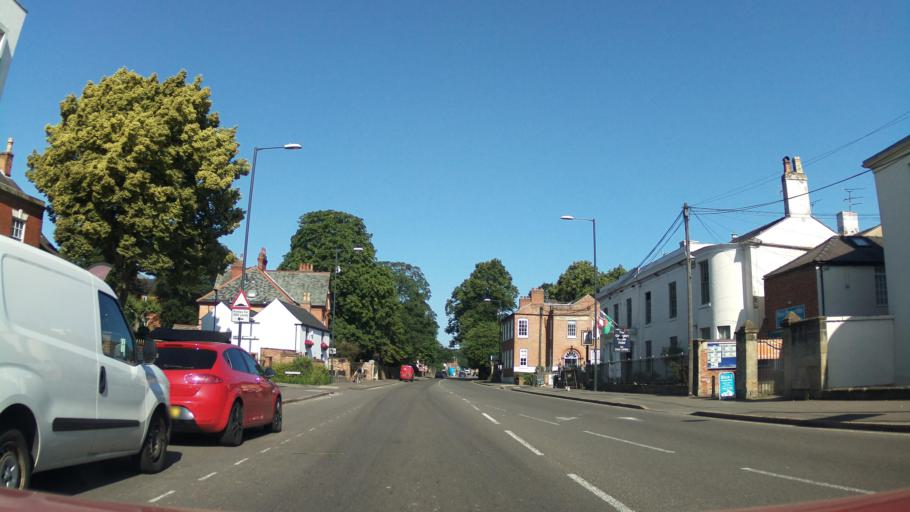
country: GB
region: England
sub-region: Derby
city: Derby
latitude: 52.9256
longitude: -1.4921
